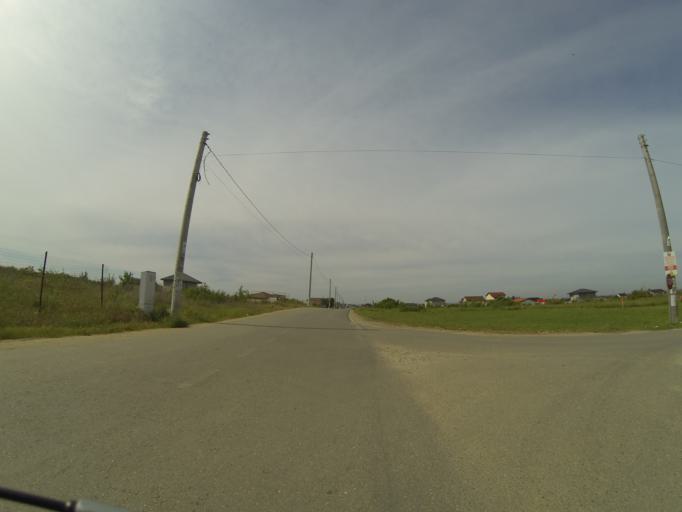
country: RO
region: Dolj
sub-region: Comuna Malu Mare
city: Preajba
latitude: 44.2876
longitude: 23.8489
